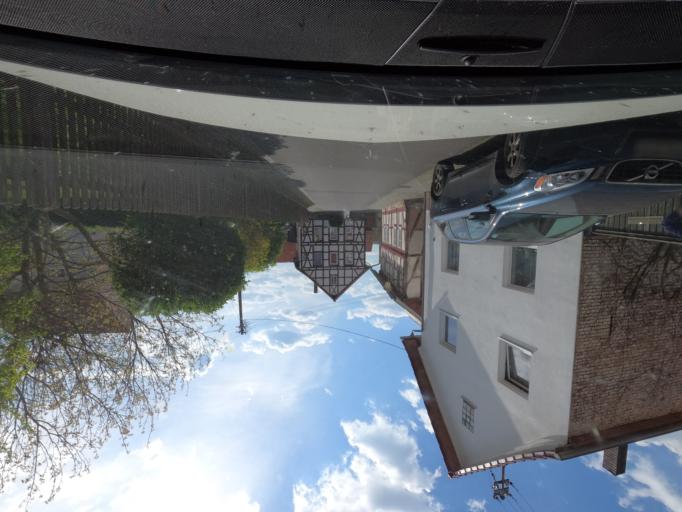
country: DE
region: Hesse
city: Wanfried
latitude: 51.1490
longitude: 10.1769
